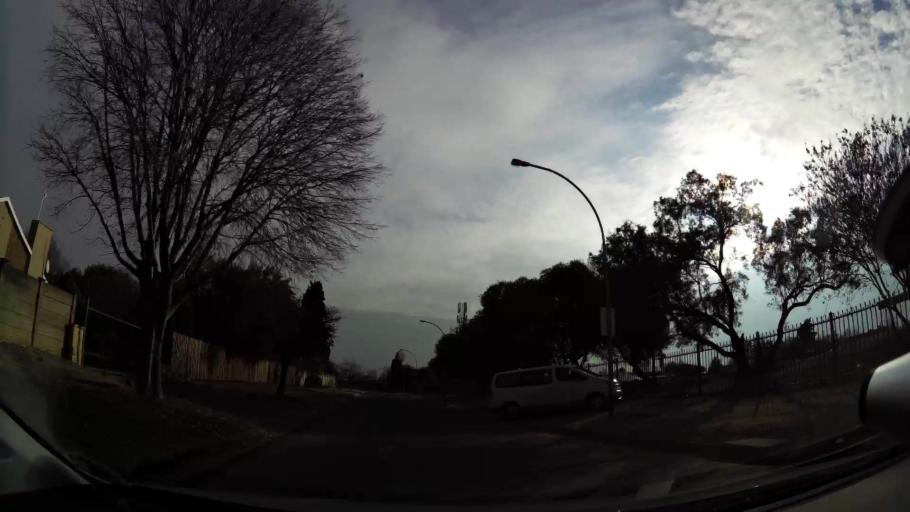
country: ZA
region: Orange Free State
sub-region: Mangaung Metropolitan Municipality
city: Bloemfontein
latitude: -29.1213
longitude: 26.1780
